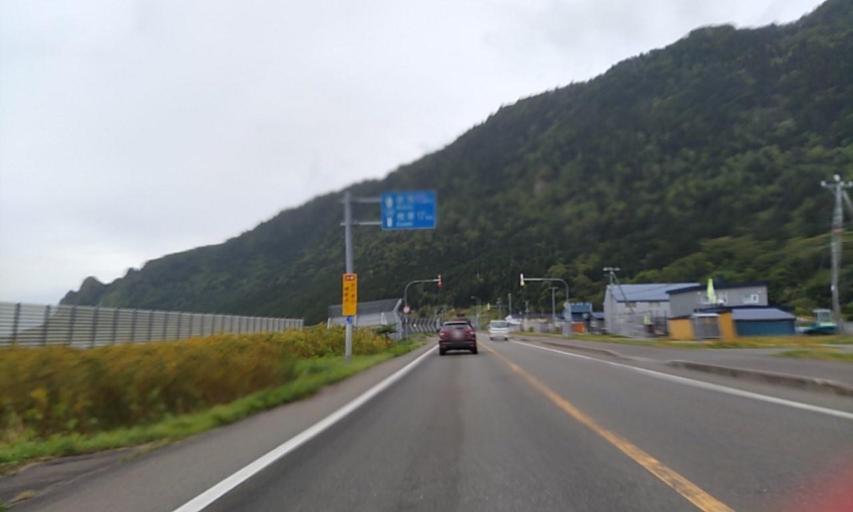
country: JP
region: Hokkaido
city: Nayoro
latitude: 45.0617
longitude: 142.4806
